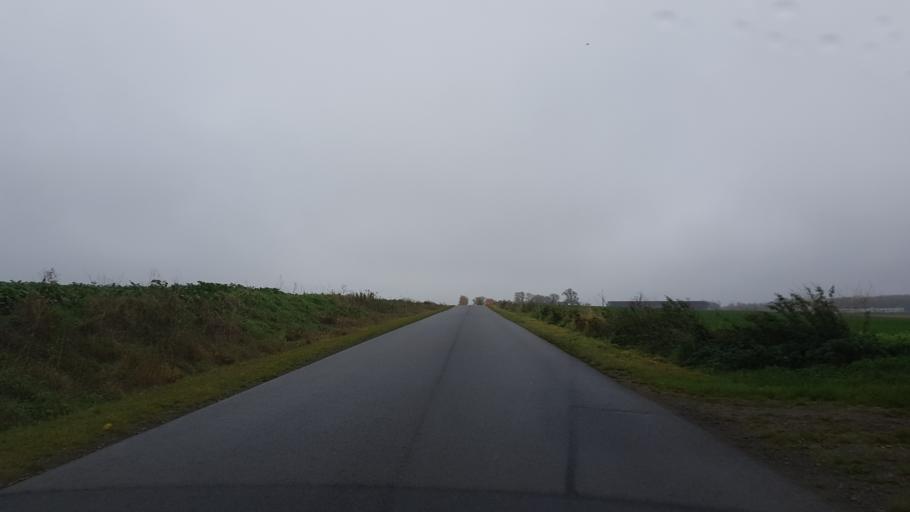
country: PL
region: West Pomeranian Voivodeship
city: Trzcinsko Zdroj
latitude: 53.0714
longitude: 14.5316
